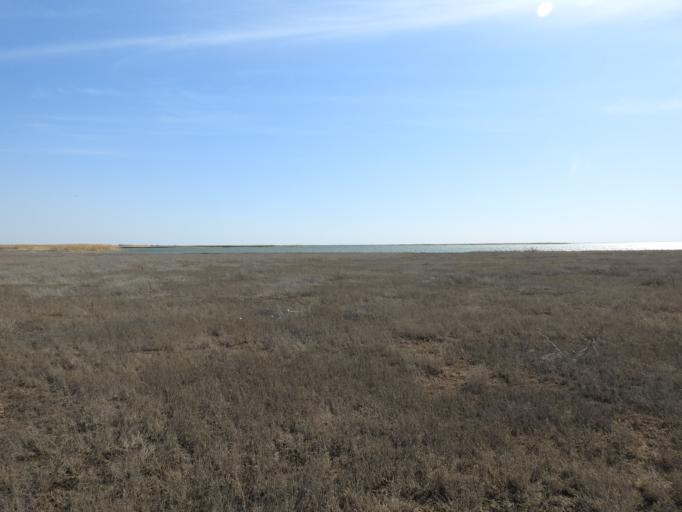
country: RU
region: Volgograd
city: Staraya Poltavka
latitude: 50.3105
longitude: 46.3636
